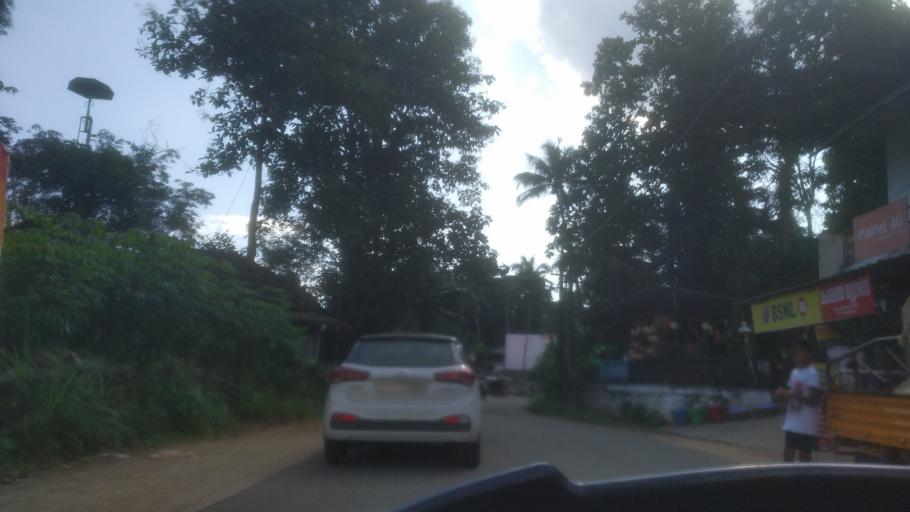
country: IN
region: Kerala
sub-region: Ernakulam
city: Muvattupula
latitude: 9.9973
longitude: 76.6139
